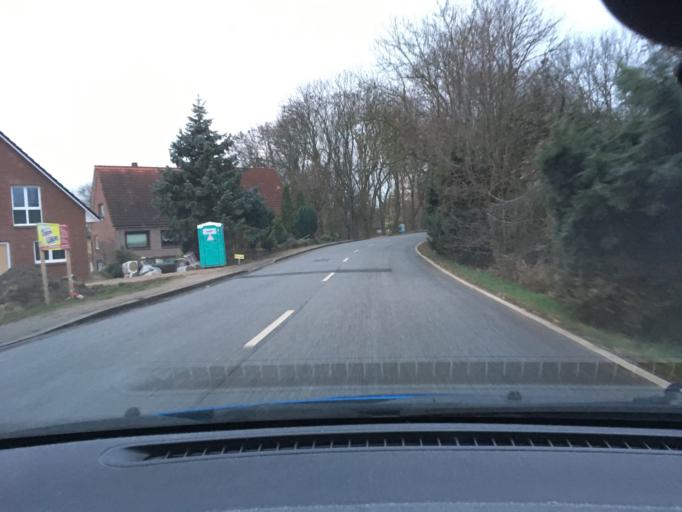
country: DE
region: Lower Saxony
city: Drage
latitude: 53.4194
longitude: 10.2043
